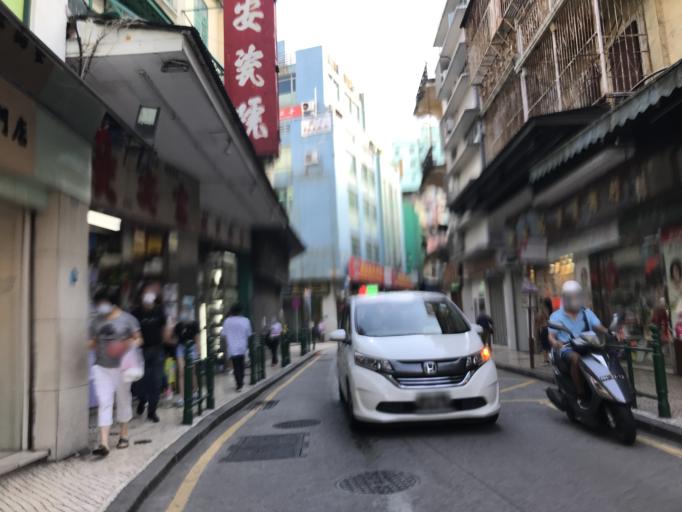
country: MO
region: Macau
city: Macau
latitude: 22.1951
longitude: 113.5399
